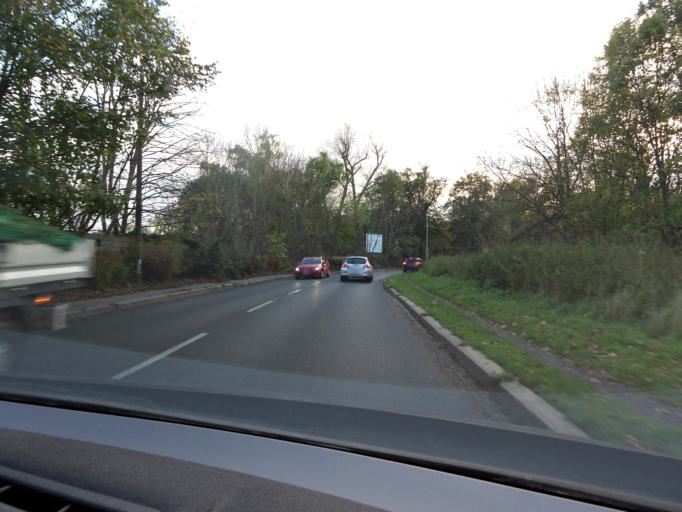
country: DE
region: Saxony
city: Leipzig
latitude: 51.3715
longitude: 12.3183
